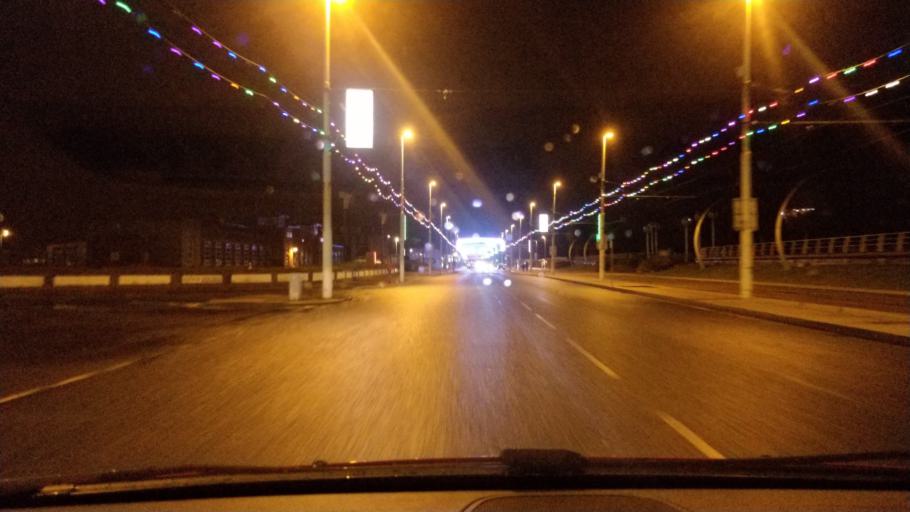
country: GB
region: England
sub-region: Blackpool
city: Blackpool
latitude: 53.7843
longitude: -3.0580
